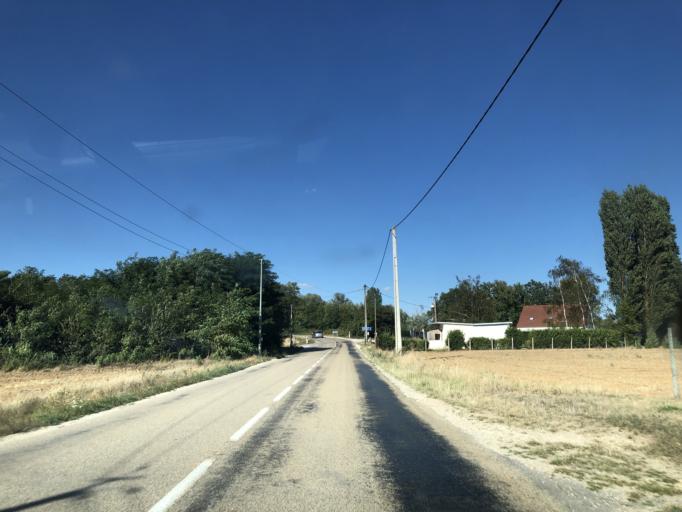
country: FR
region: Bourgogne
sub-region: Departement de l'Yonne
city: Appoigny
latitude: 47.8845
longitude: 3.5423
